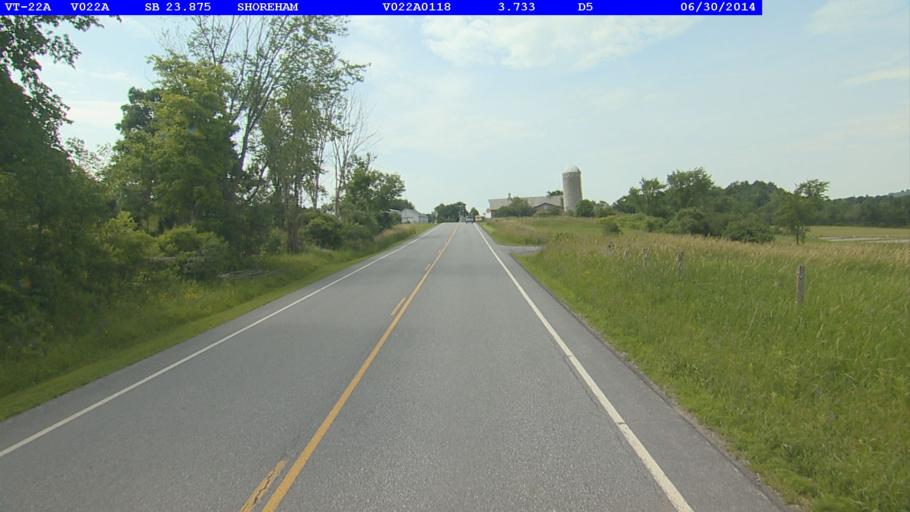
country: US
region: New York
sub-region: Essex County
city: Ticonderoga
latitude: 43.9034
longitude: -73.3082
